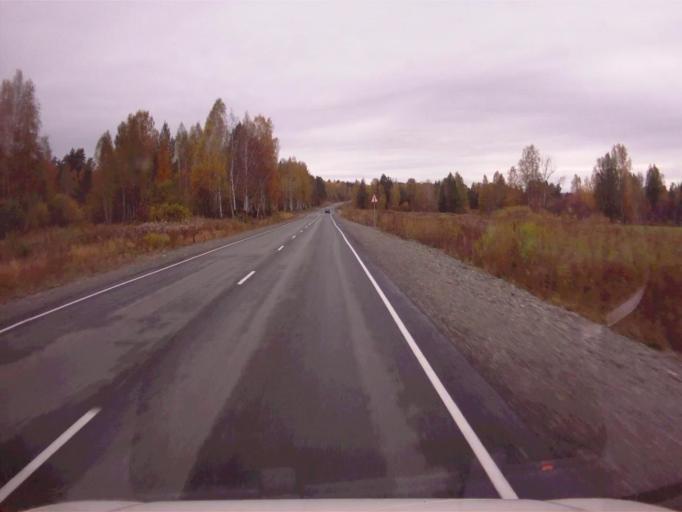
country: RU
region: Chelyabinsk
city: Nyazepetrovsk
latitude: 56.0447
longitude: 59.7640
